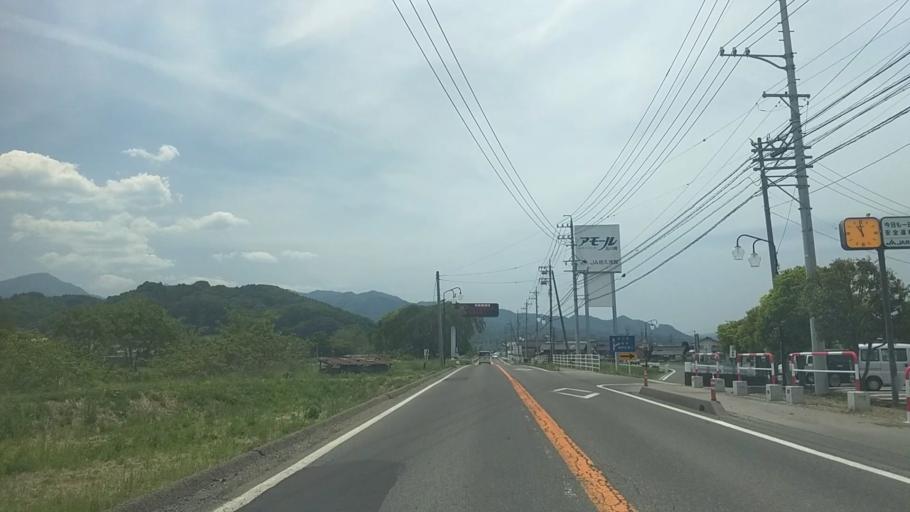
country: JP
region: Nagano
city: Saku
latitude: 36.1716
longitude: 138.4857
